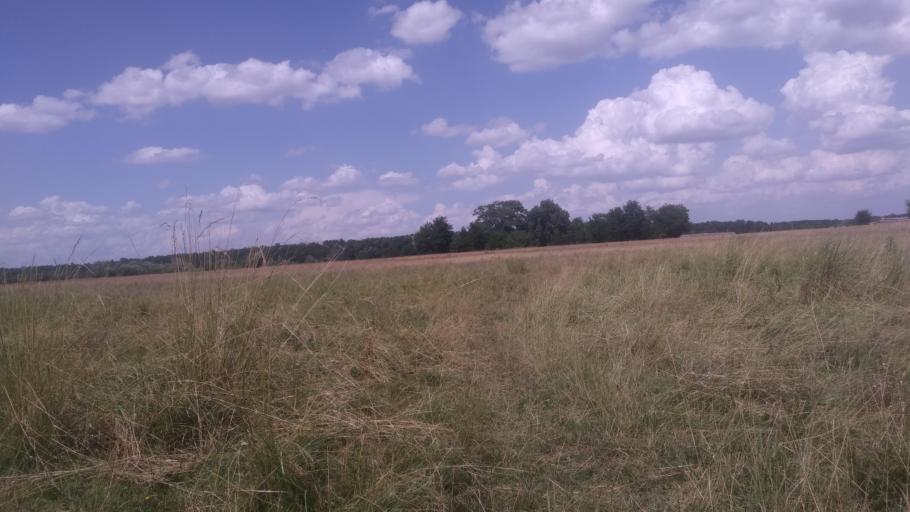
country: HU
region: Pest
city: Cegledbercel
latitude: 47.1856
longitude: 19.7256
